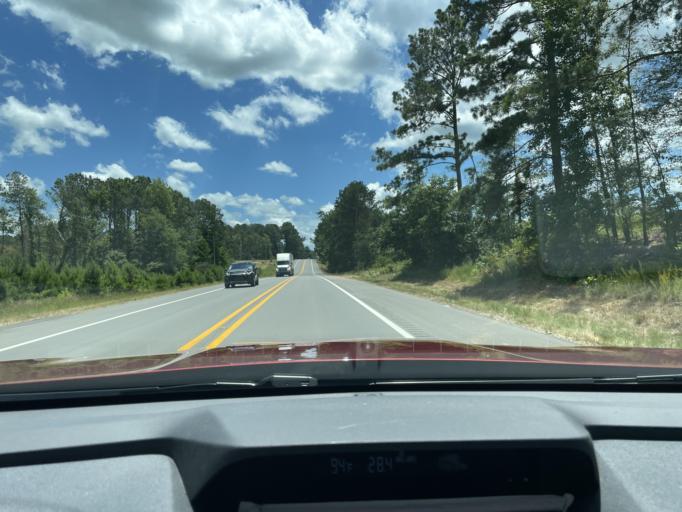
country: US
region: Arkansas
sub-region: Drew County
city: Monticello
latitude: 33.7327
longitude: -91.8155
